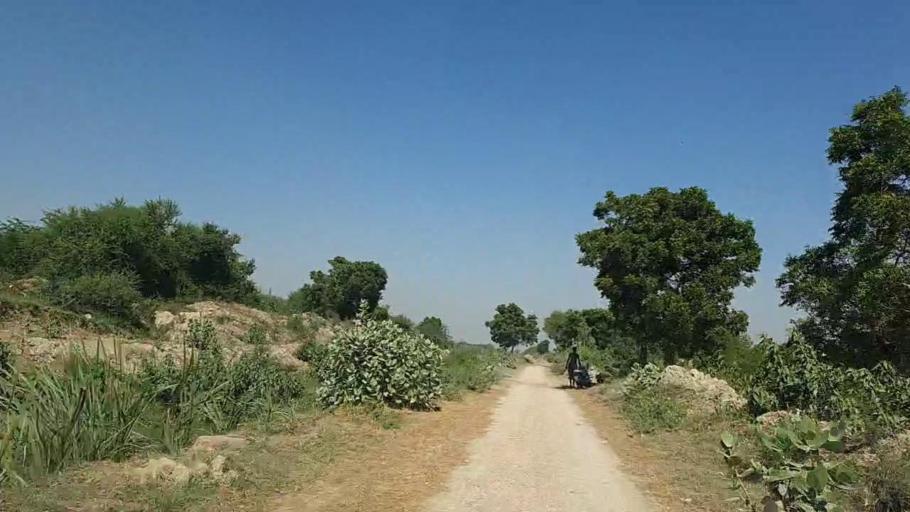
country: PK
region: Sindh
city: Daro Mehar
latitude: 24.7558
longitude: 68.1590
